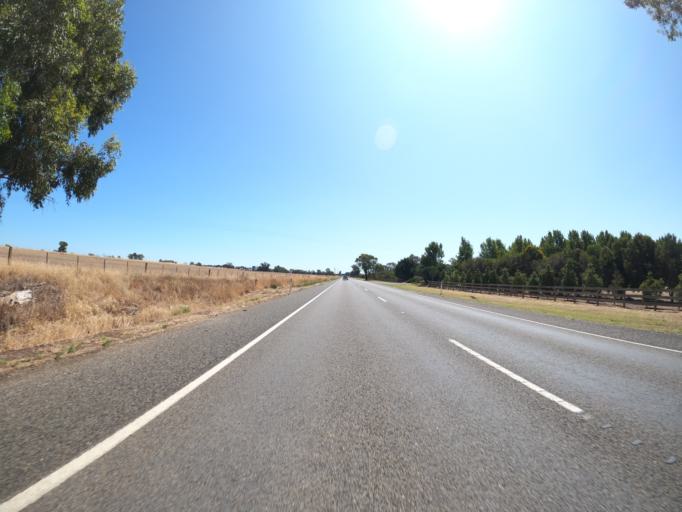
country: AU
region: Victoria
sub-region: Moira
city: Yarrawonga
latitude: -36.0260
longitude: 146.0925
